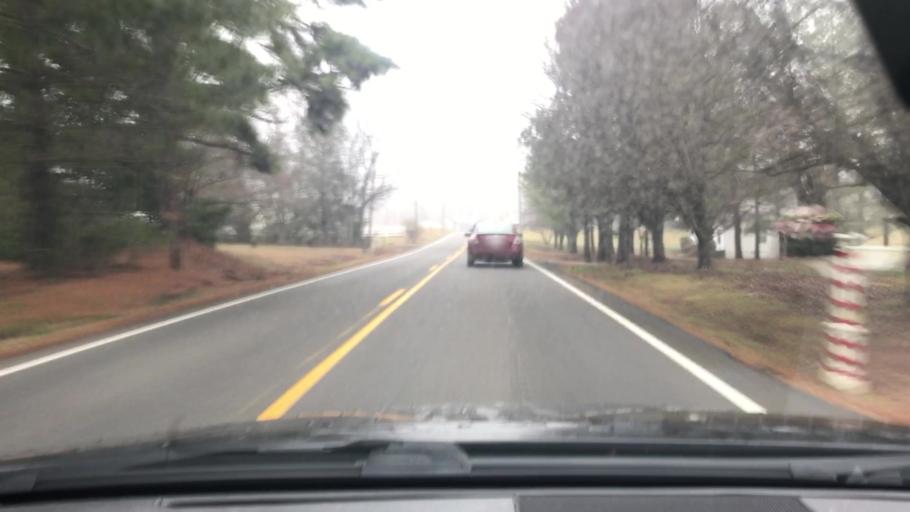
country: US
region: Tennessee
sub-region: Cheatham County
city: Ashland City
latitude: 36.2855
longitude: -87.1720
